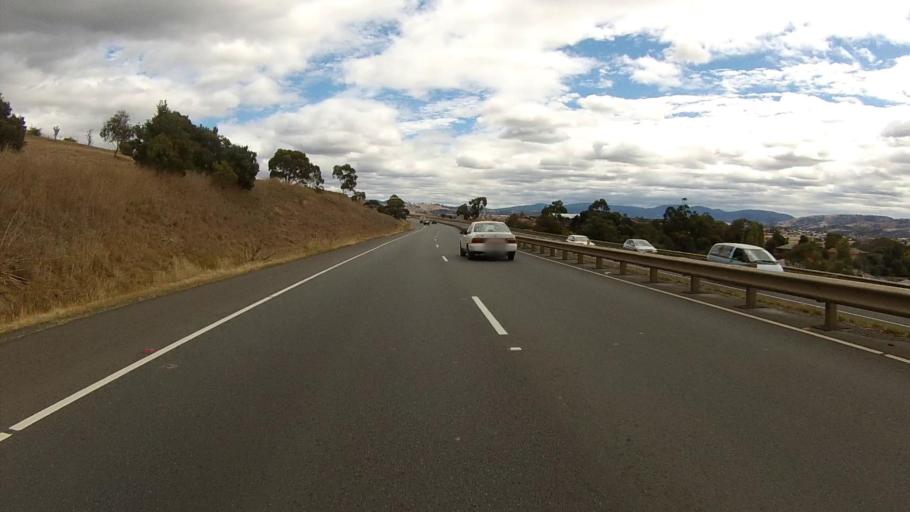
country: AU
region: Tasmania
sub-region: Glenorchy
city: Austins Ferry
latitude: -42.7667
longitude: 147.2355
